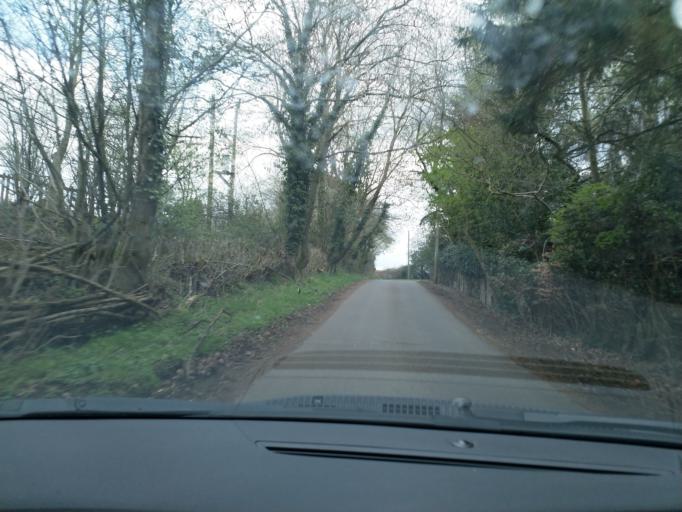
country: GB
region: England
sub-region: Warwickshire
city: Henley in Arden
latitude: 52.2884
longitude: -1.7311
